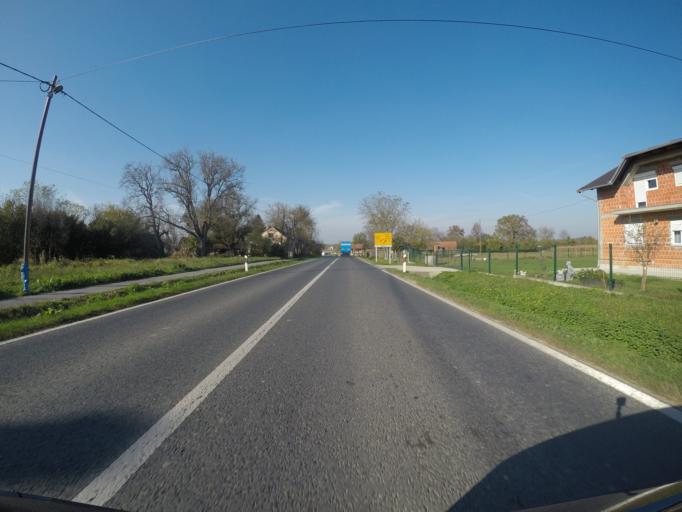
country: HR
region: Bjelovarsko-Bilogorska
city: Predavac
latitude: 45.9305
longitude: 16.7855
